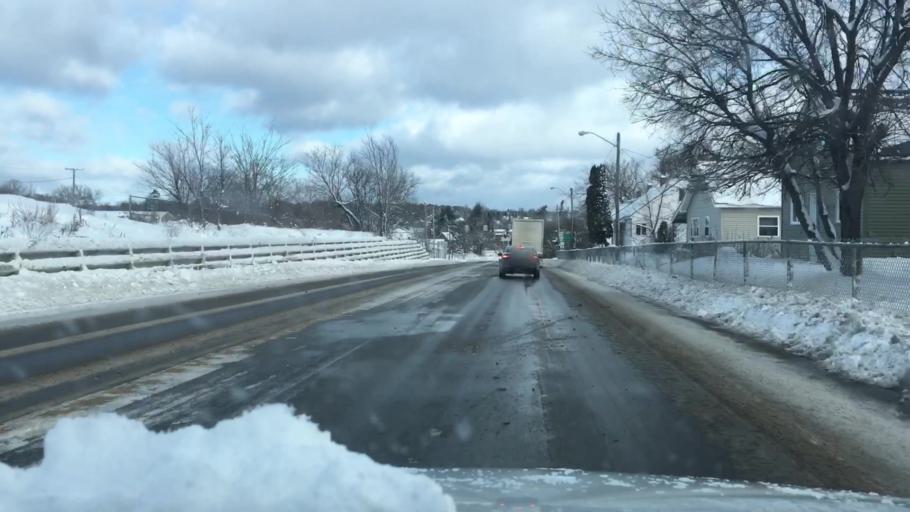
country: US
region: Maine
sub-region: Aroostook County
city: Caribou
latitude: 46.8523
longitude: -68.0054
